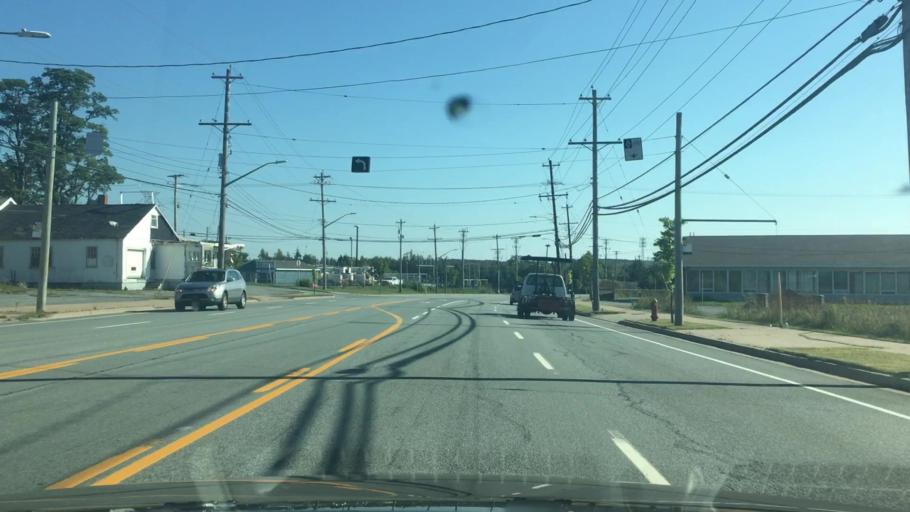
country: CA
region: Nova Scotia
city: Cole Harbour
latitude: 44.6997
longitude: -63.4839
